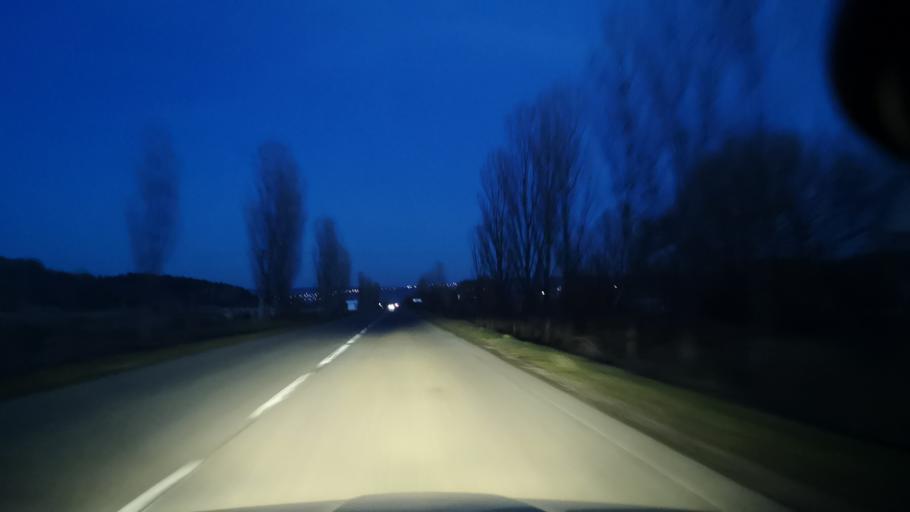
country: MD
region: Orhei
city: Orhei
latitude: 47.3439
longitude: 28.7444
